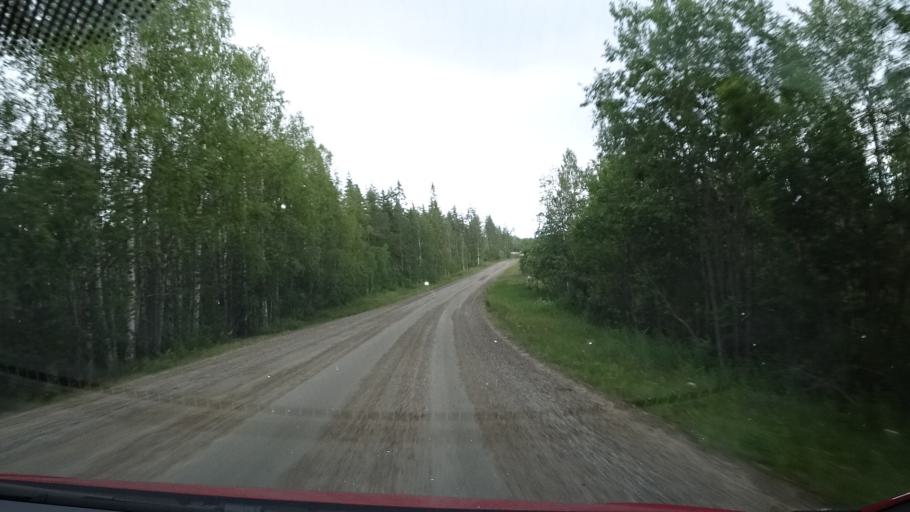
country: FI
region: Kainuu
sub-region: Kehys-Kainuu
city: Kuhmo
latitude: 63.9526
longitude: 29.2254
